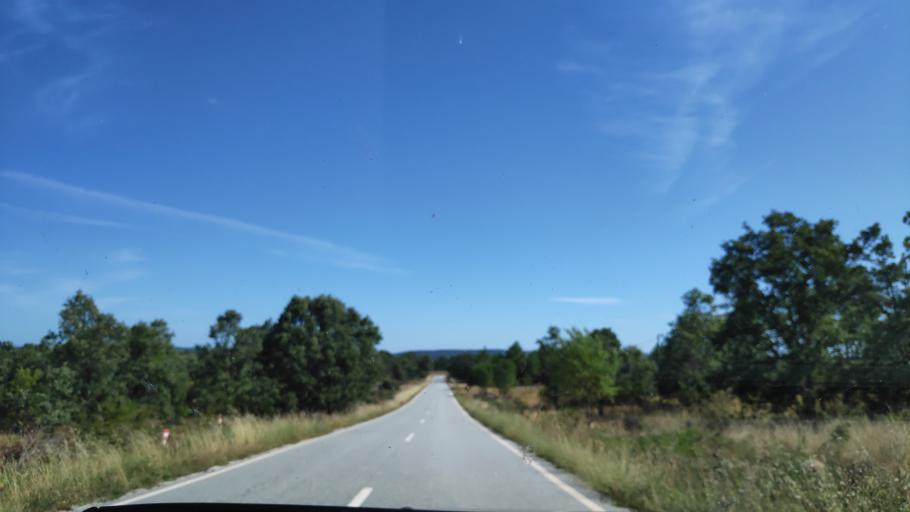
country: ES
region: Castille and Leon
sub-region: Provincia de Zamora
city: Alcanices
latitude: 41.6122
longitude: -6.3463
